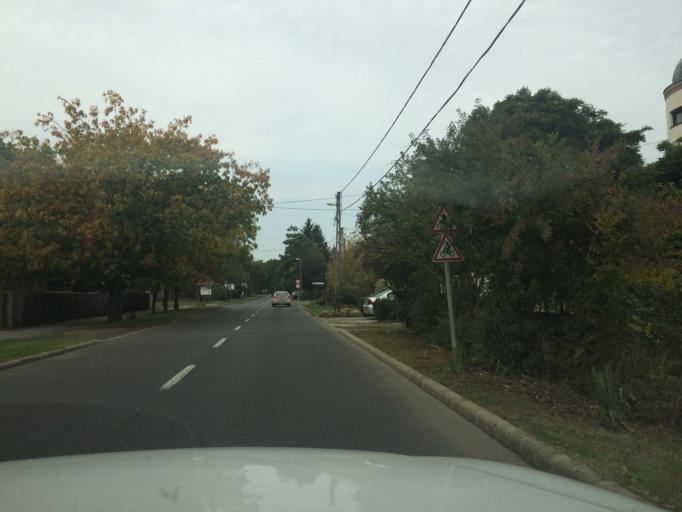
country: HU
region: Szabolcs-Szatmar-Bereg
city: Kotaj
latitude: 48.0089
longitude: 21.7337
